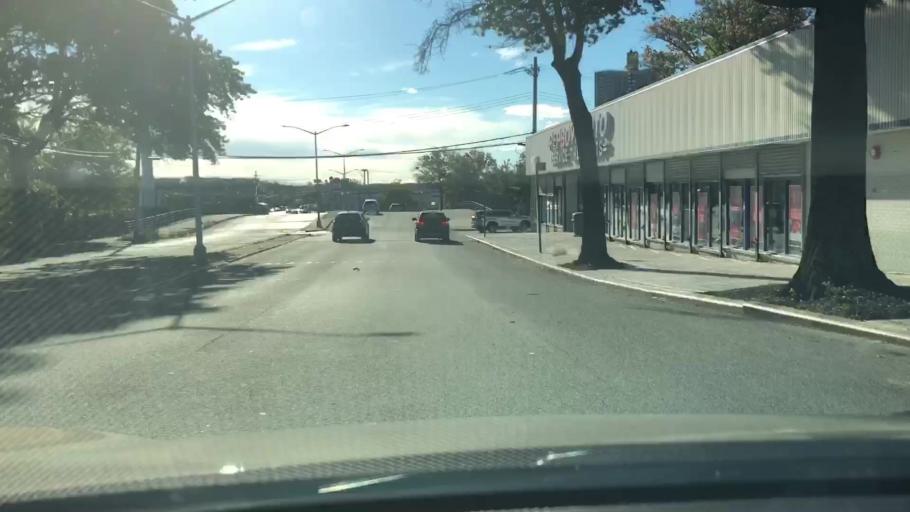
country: US
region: New York
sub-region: Bronx
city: Eastchester
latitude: 40.8846
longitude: -73.8266
